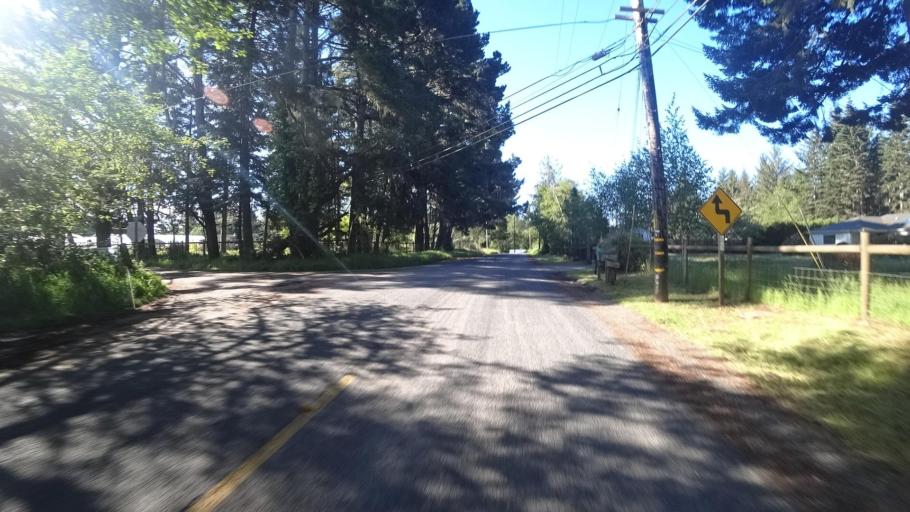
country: US
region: California
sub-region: Humboldt County
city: Westhaven-Moonstone
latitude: 40.9983
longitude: -124.1006
